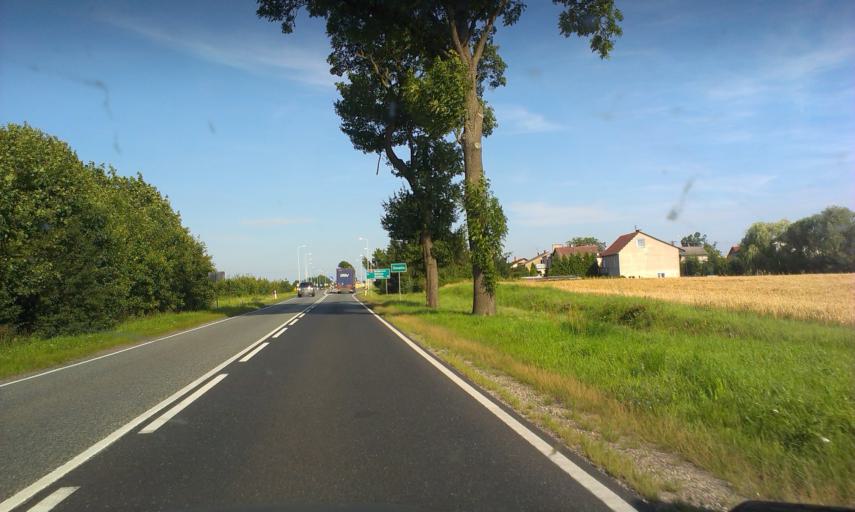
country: PL
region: Kujawsko-Pomorskie
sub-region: Powiat nakielski
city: Sadki
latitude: 53.1532
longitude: 17.4840
